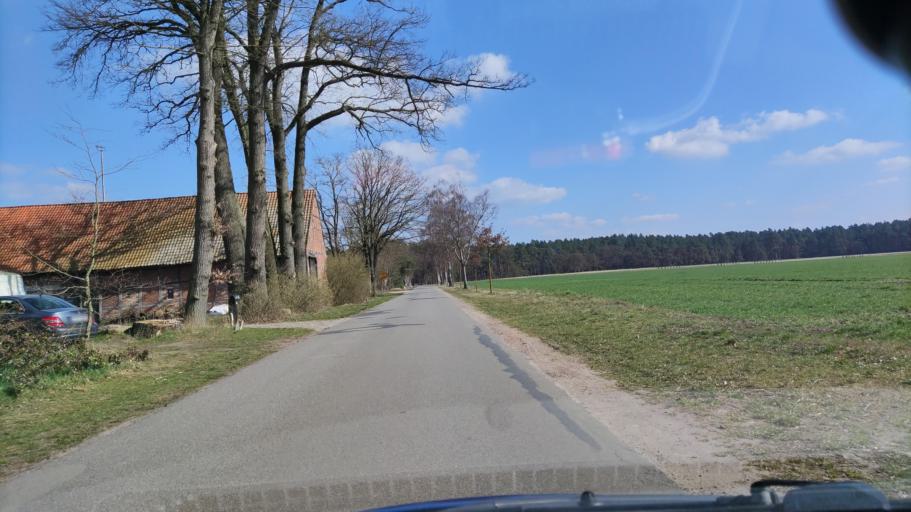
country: DE
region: Lower Saxony
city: Trebel
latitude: 53.0043
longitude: 11.2762
